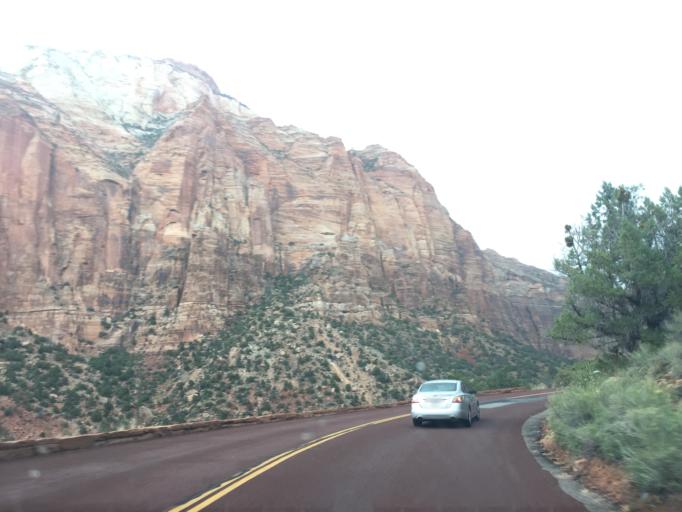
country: US
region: Utah
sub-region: Washington County
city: Hildale
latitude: 37.2146
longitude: -112.9620
